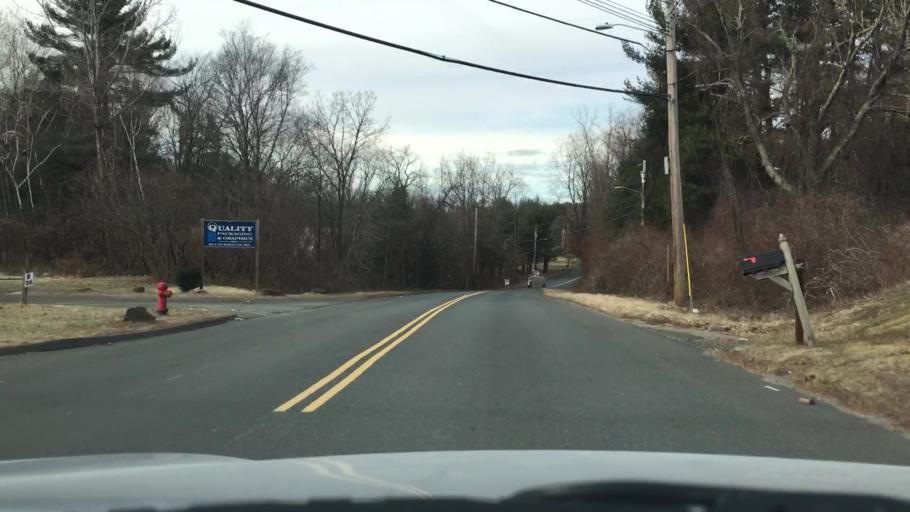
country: US
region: Massachusetts
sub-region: Hampden County
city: Westfield
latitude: 42.1426
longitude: -72.7378
